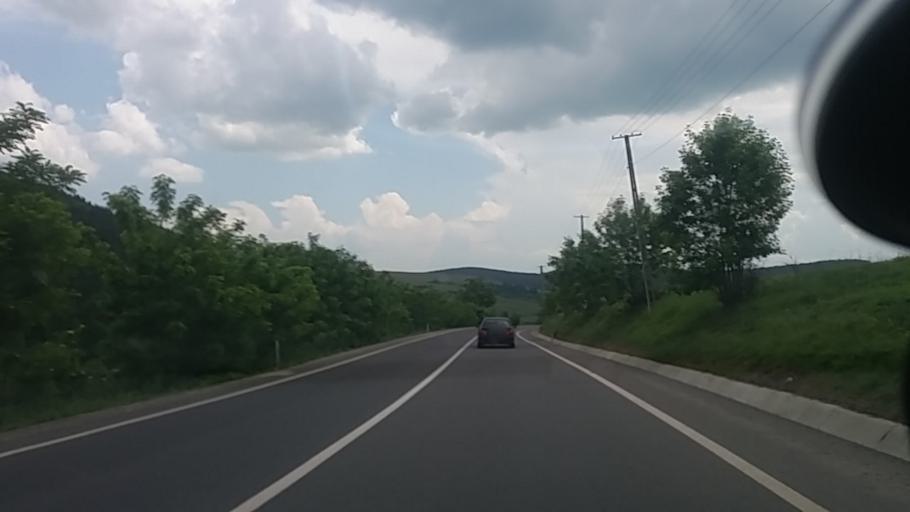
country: RO
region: Sibiu
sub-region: Comuna Slimnic
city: Slimnic
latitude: 45.9306
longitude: 24.1700
